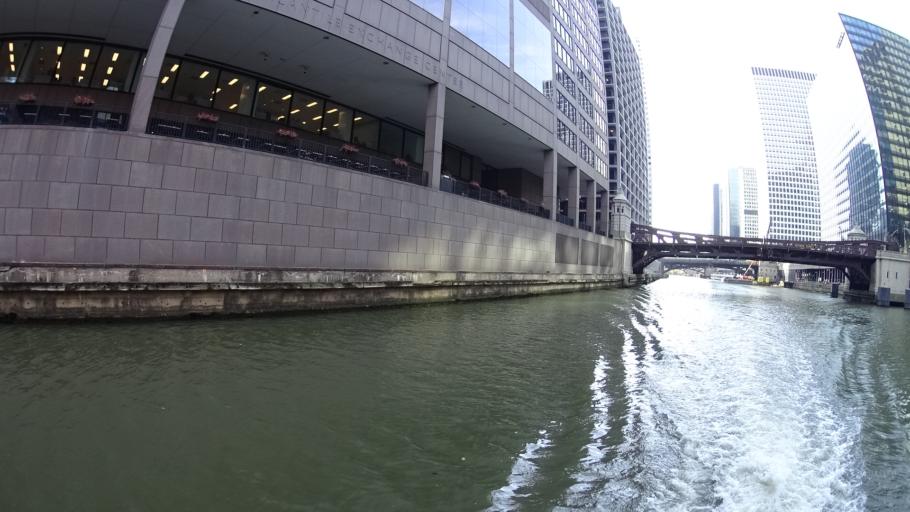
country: US
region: Illinois
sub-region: Cook County
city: Chicago
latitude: 41.8812
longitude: -87.6381
